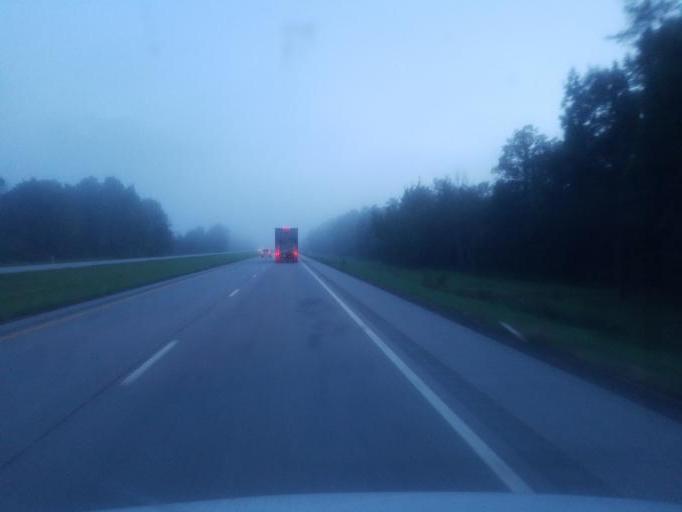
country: US
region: Ohio
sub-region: Ashtabula County
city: Jefferson
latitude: 41.6602
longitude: -80.7133
